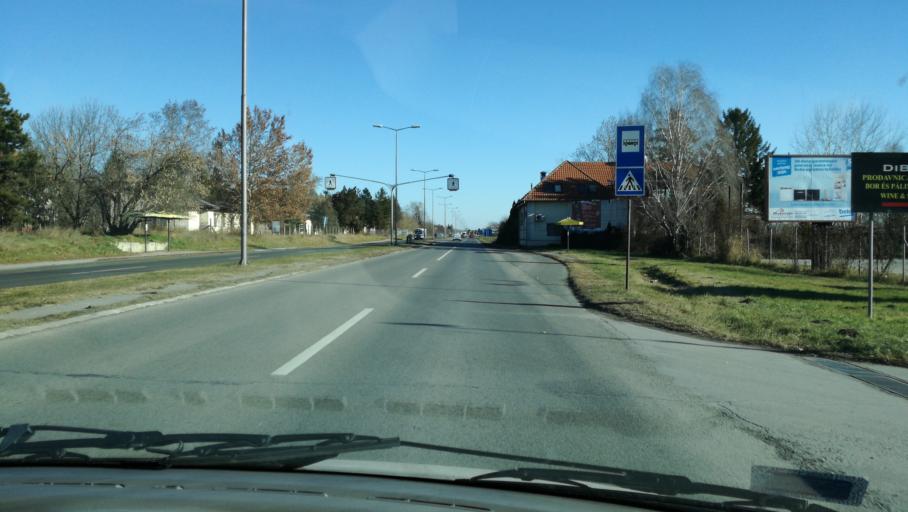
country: RS
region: Autonomna Pokrajina Vojvodina
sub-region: Severnobacki Okrug
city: Subotica
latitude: 46.1034
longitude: 19.7122
